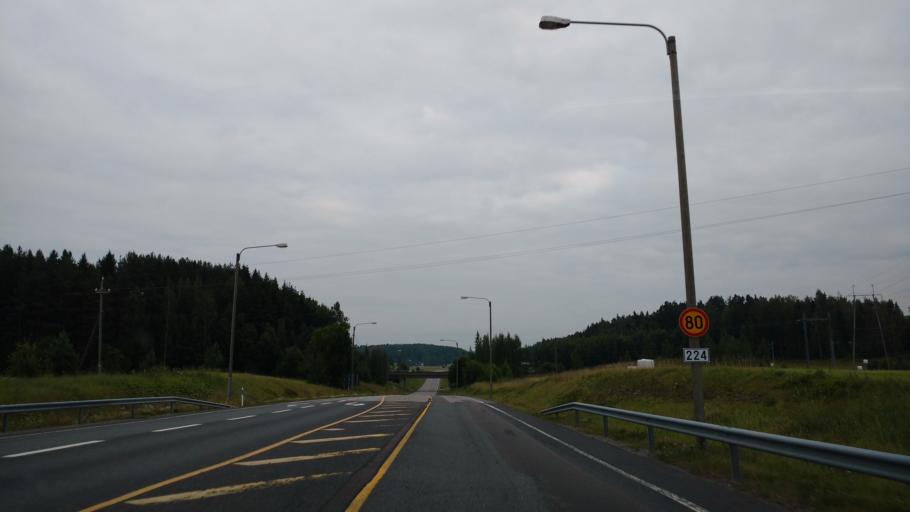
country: FI
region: Varsinais-Suomi
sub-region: Salo
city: Halikko
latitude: 60.3990
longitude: 23.0517
